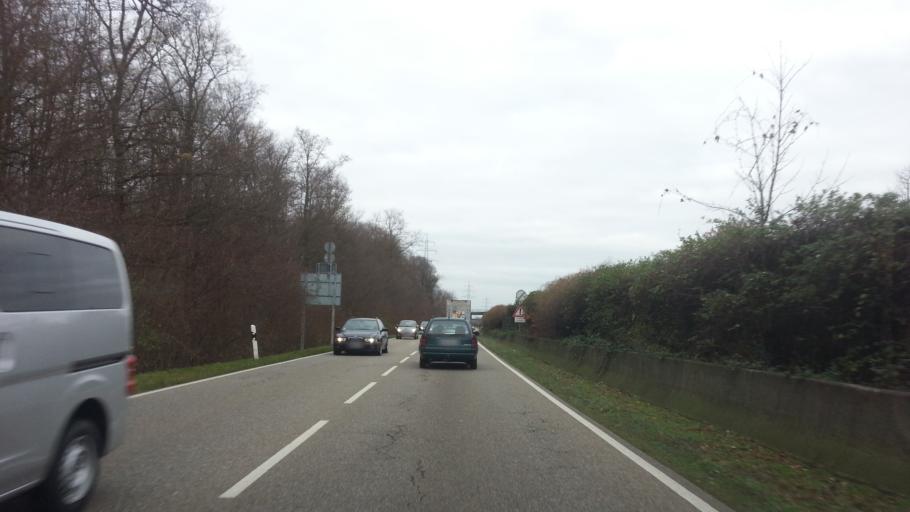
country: DE
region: Baden-Wuerttemberg
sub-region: Karlsruhe Region
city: Ketsch
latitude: 49.3778
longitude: 8.5466
